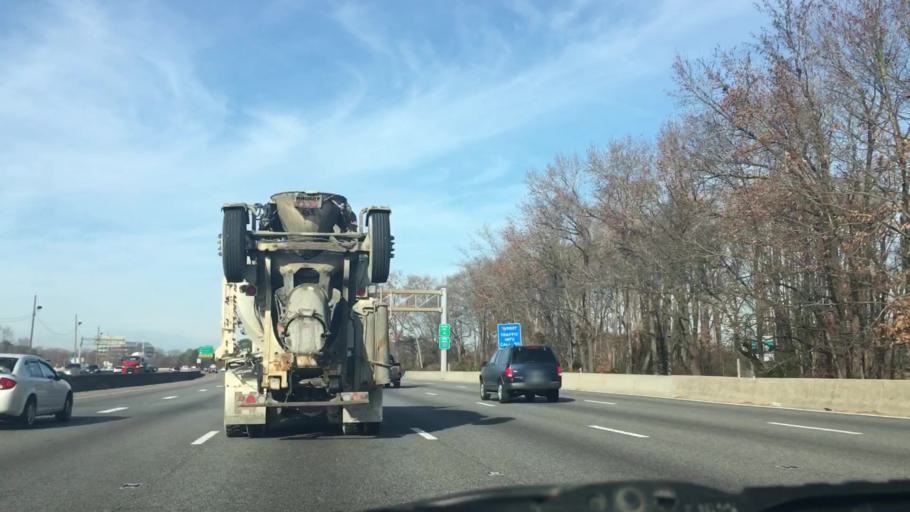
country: US
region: Virginia
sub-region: City of Chesapeake
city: Chesapeake
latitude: 36.8433
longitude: -76.1670
